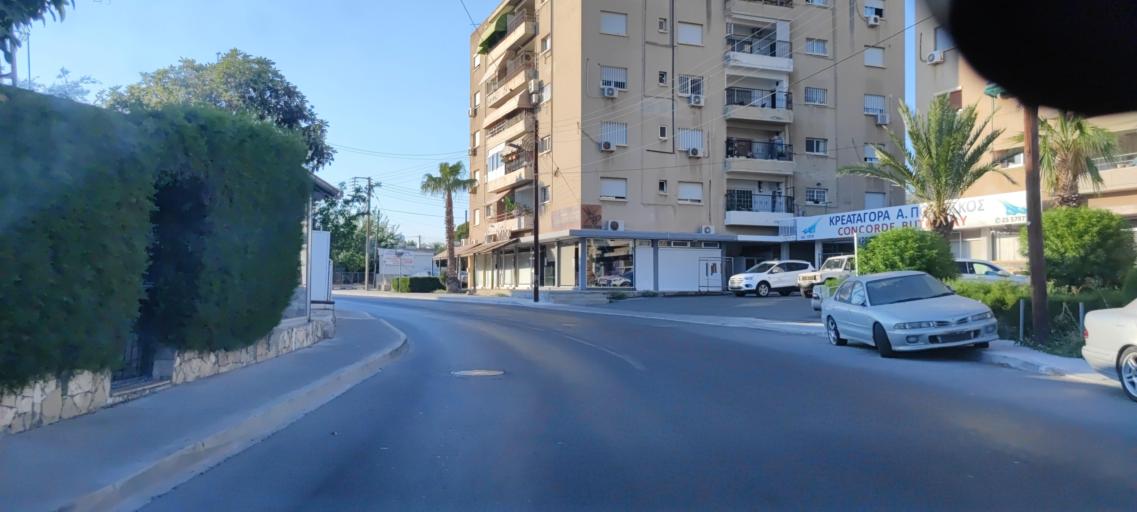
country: CY
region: Limassol
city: Limassol
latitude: 34.6778
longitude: 33.0288
